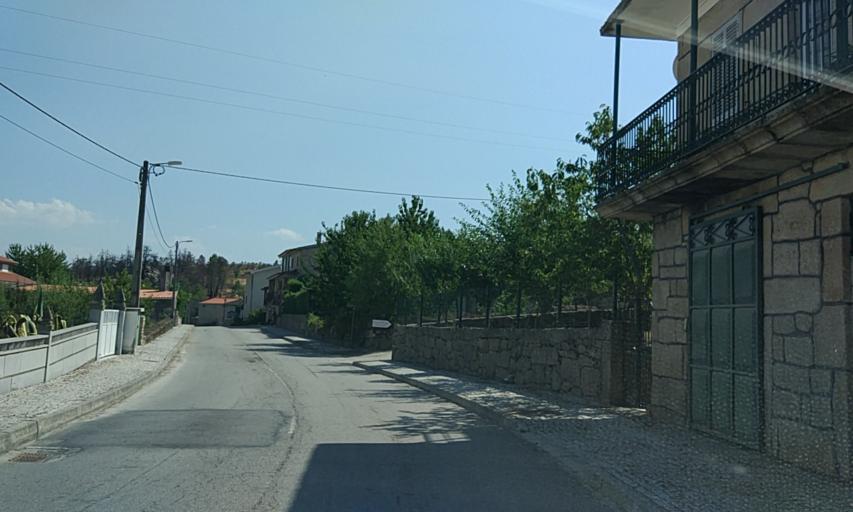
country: PT
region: Vila Real
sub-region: Murca
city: Murca
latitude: 41.3751
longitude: -7.5036
